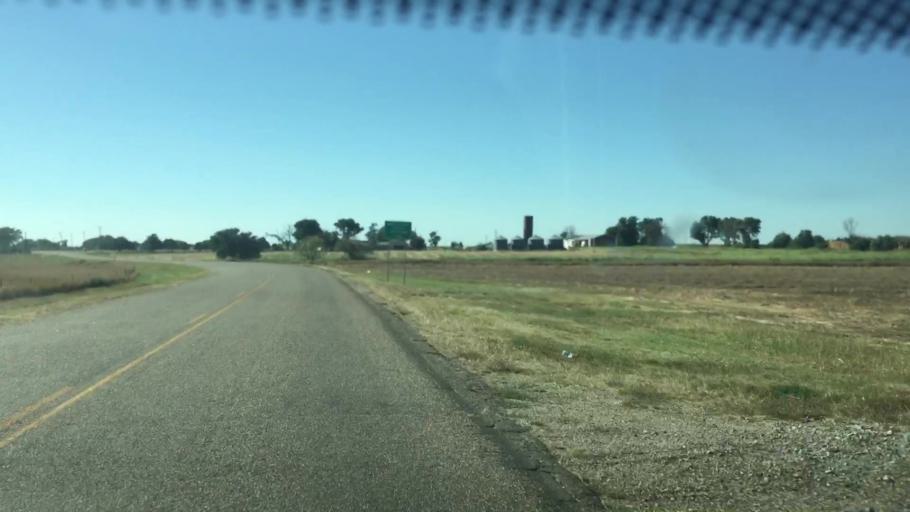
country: US
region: Colorado
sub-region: Prowers County
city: Lamar
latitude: 38.1175
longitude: -102.6090
